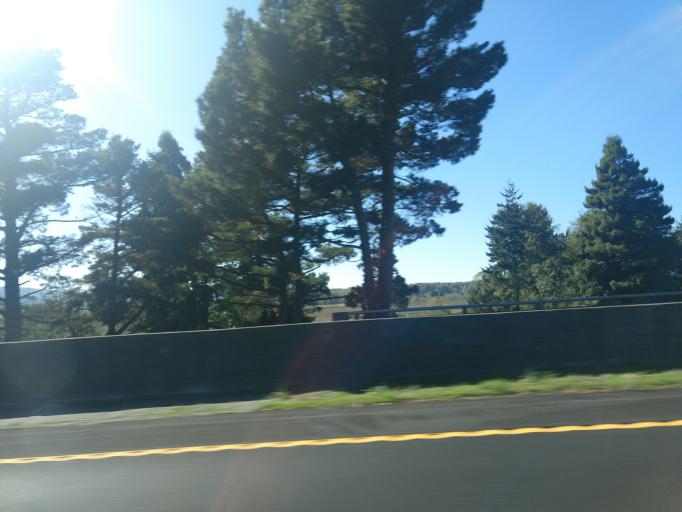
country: US
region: California
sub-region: Humboldt County
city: Fortuna
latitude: 40.5745
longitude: -124.1489
